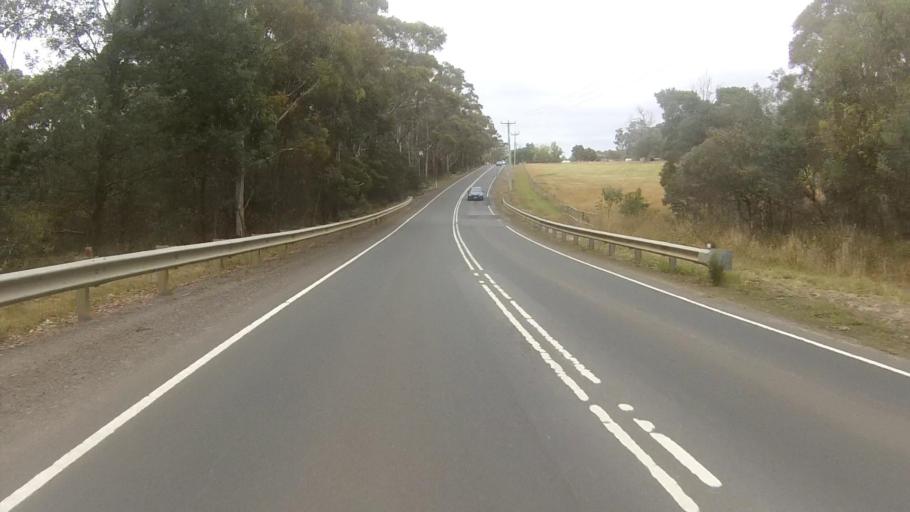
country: AU
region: Tasmania
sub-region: Kingborough
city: Margate
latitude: -42.9858
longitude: 147.1966
